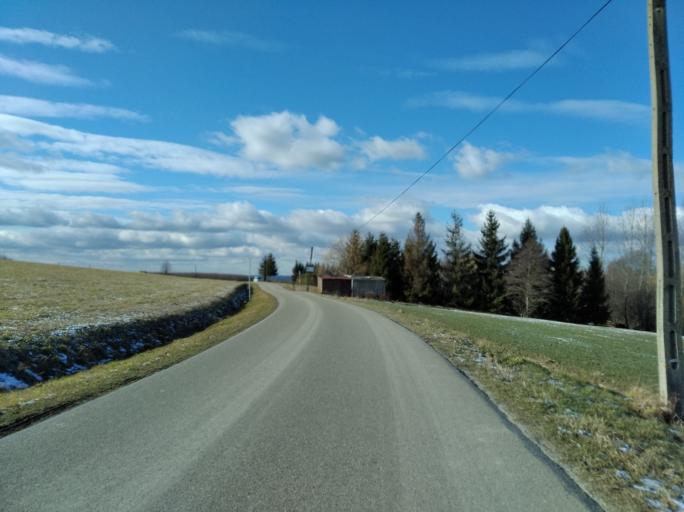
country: PL
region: Subcarpathian Voivodeship
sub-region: Powiat ropczycko-sedziszowski
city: Wielopole Skrzynskie
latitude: 49.9165
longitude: 21.6344
